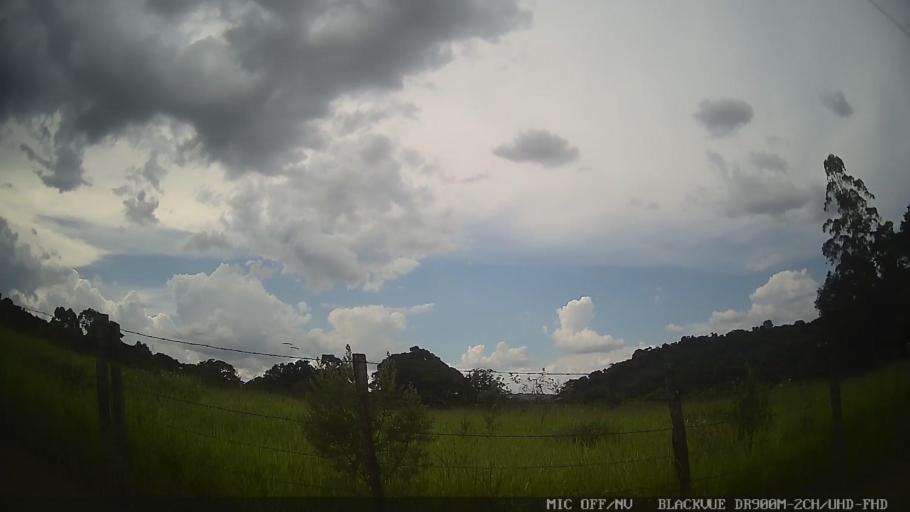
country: BR
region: Sao Paulo
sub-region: Atibaia
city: Atibaia
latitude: -23.1608
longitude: -46.5707
